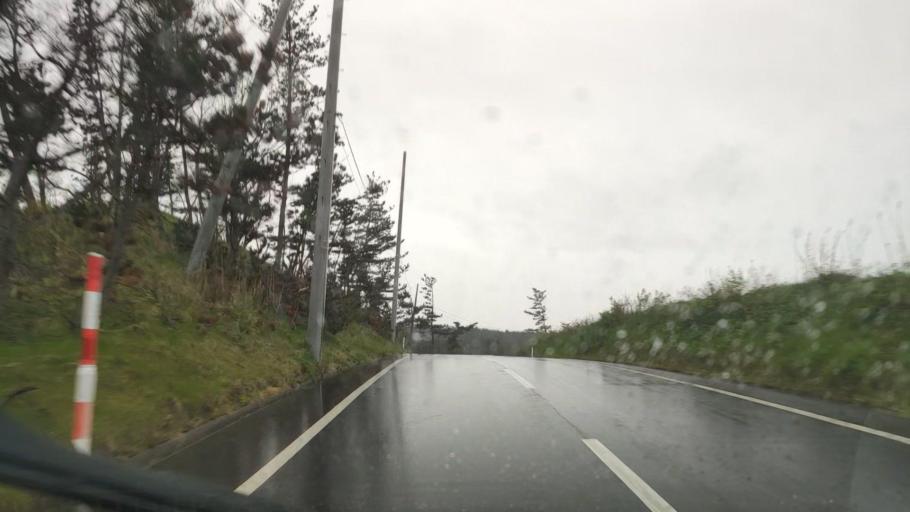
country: JP
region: Akita
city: Noshiromachi
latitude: 40.0762
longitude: 139.9516
